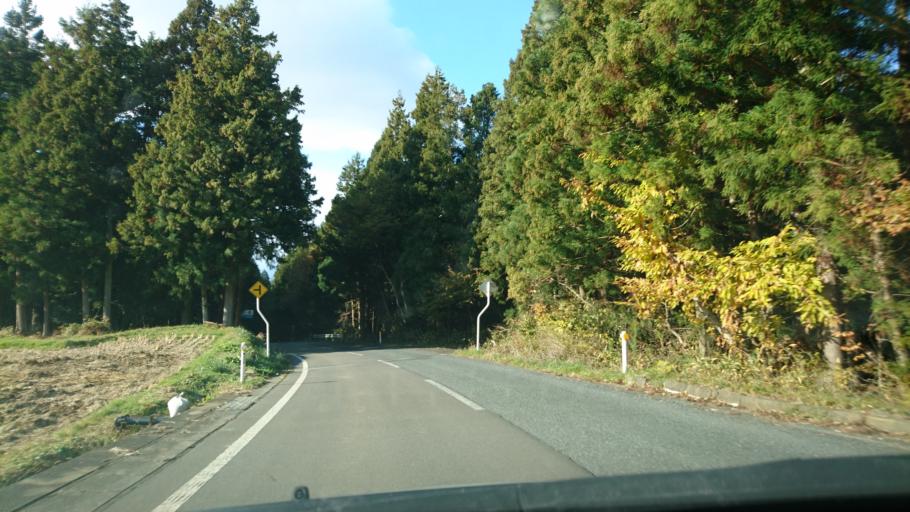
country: JP
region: Iwate
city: Mizusawa
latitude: 39.0320
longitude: 141.1603
